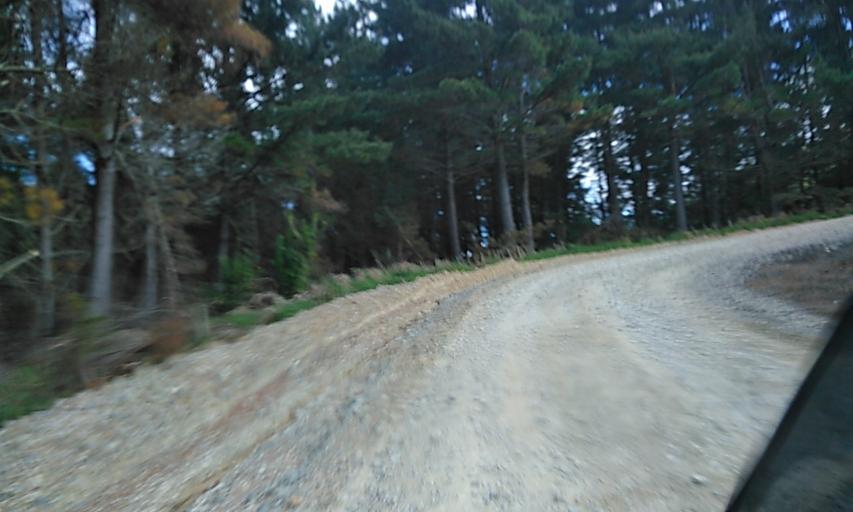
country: NZ
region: Gisborne
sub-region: Gisborne District
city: Gisborne
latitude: -38.3254
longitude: 178.0732
